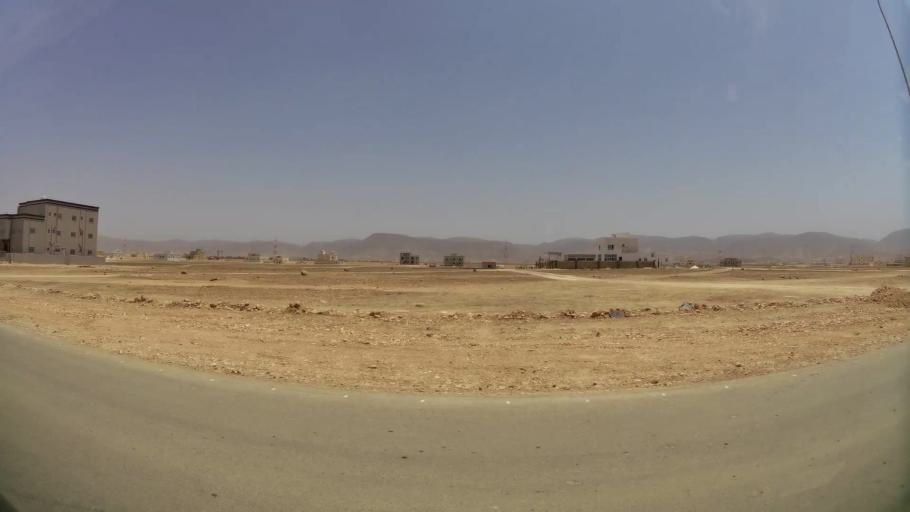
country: OM
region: Zufar
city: Salalah
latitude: 17.0979
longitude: 54.1993
